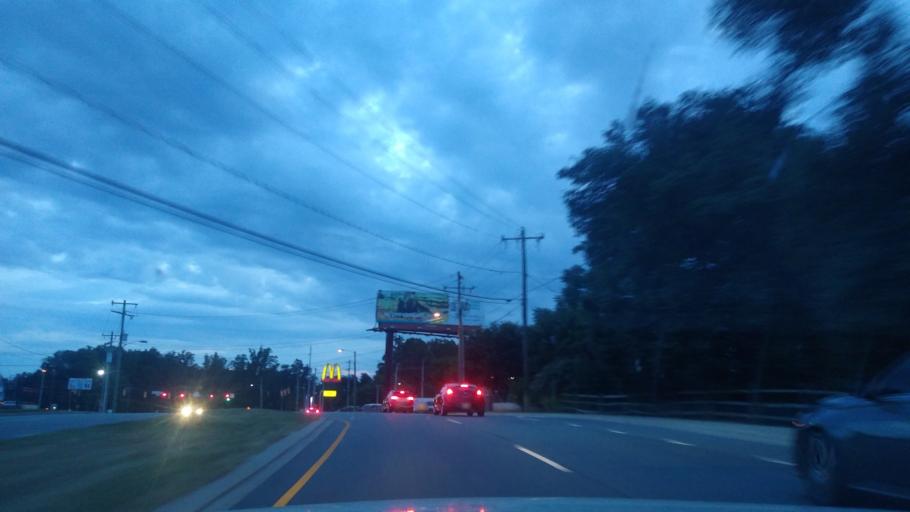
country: US
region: North Carolina
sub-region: Guilford County
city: Greensboro
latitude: 36.1088
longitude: -79.8266
